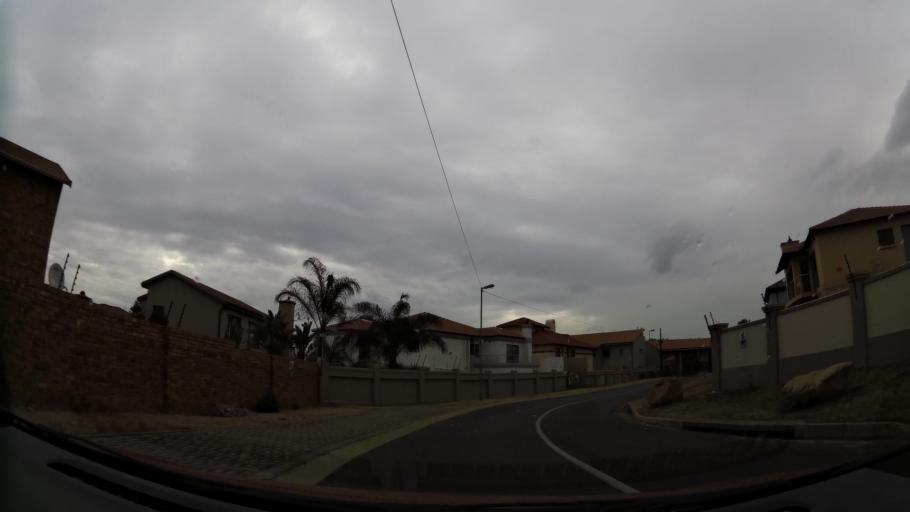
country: ZA
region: Gauteng
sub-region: City of Johannesburg Metropolitan Municipality
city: Roodepoort
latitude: -26.1147
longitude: 27.9112
